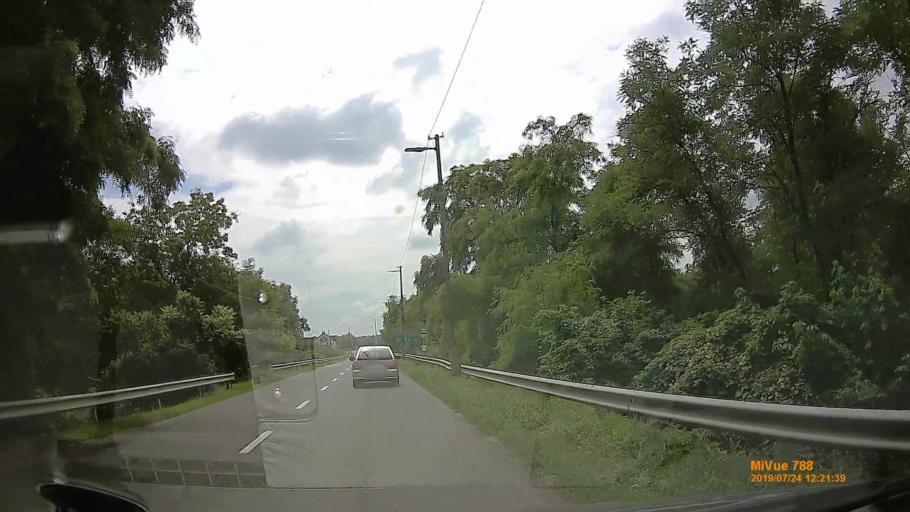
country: HU
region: Szabolcs-Szatmar-Bereg
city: Vasarosnameny
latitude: 48.1281
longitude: 22.3417
